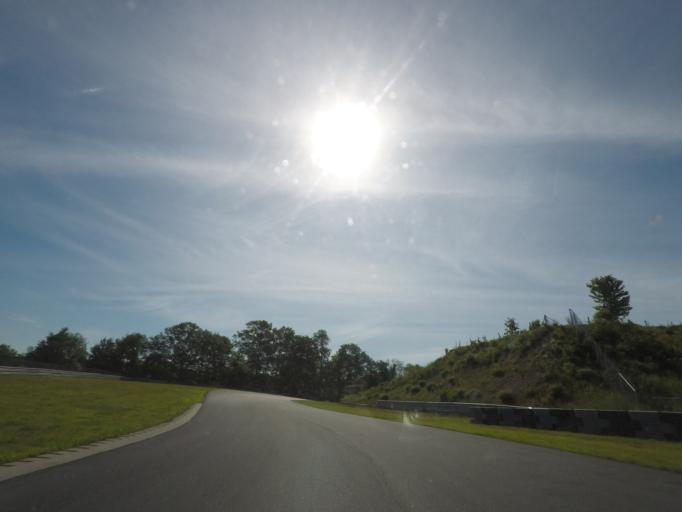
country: US
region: Connecticut
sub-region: Windham County
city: Thompson
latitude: 41.9803
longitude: -71.8233
